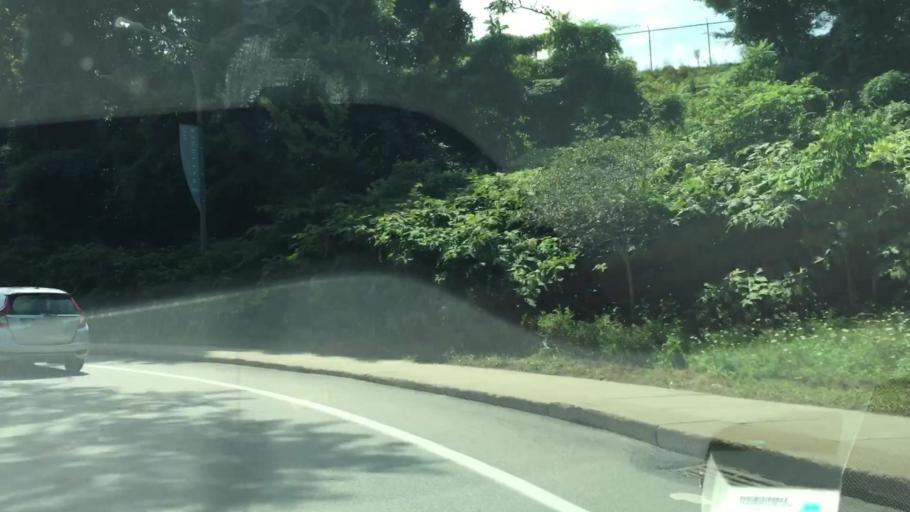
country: US
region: Pennsylvania
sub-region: Allegheny County
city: Sharpsburg
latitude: 40.4815
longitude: -79.9201
